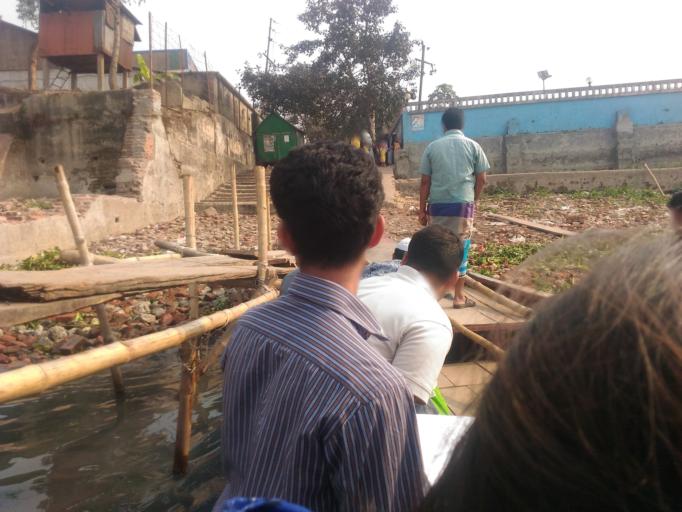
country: BD
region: Dhaka
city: Narayanganj
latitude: 23.6314
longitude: 90.4606
